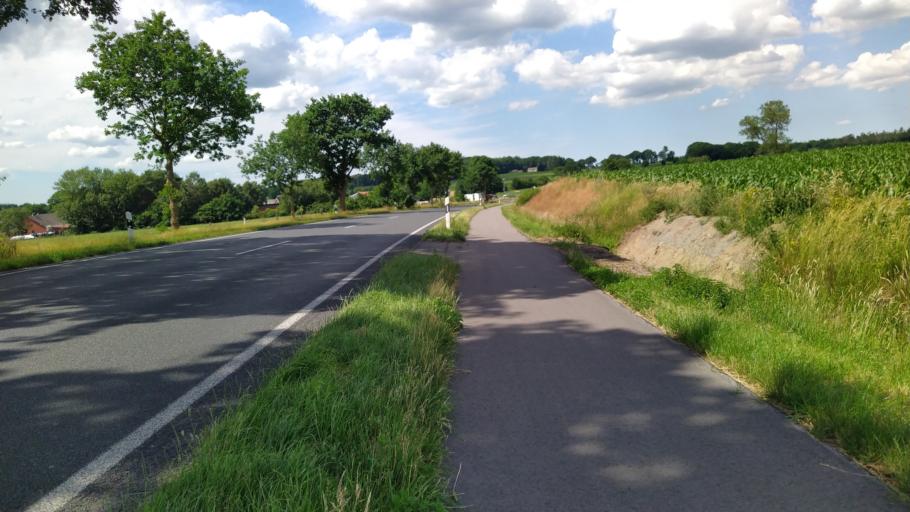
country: DE
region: Lower Saxony
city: Armstorf
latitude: 53.5969
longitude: 9.0822
